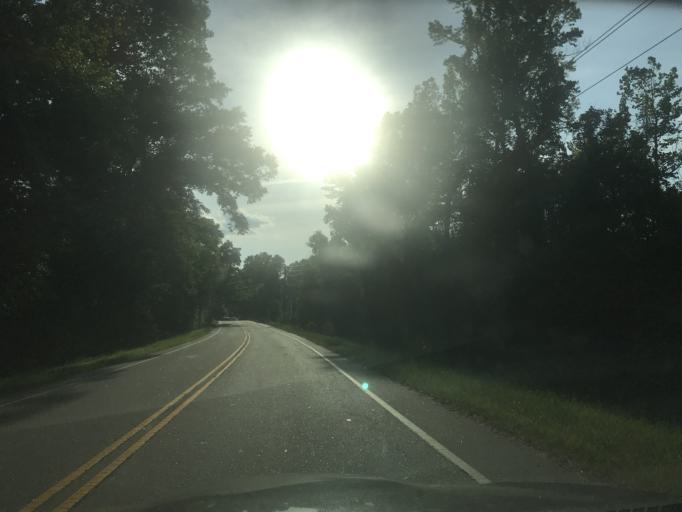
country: US
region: North Carolina
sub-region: Wake County
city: Knightdale
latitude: 35.7546
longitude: -78.5303
